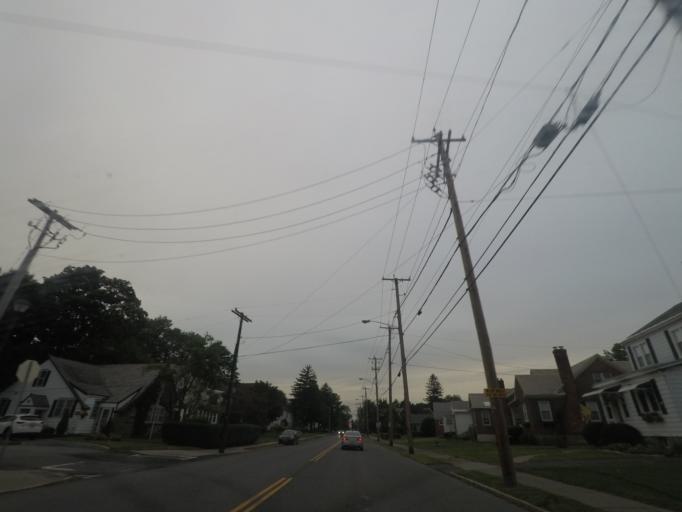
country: US
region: New York
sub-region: Albany County
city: Albany
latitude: 42.6449
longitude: -73.7946
